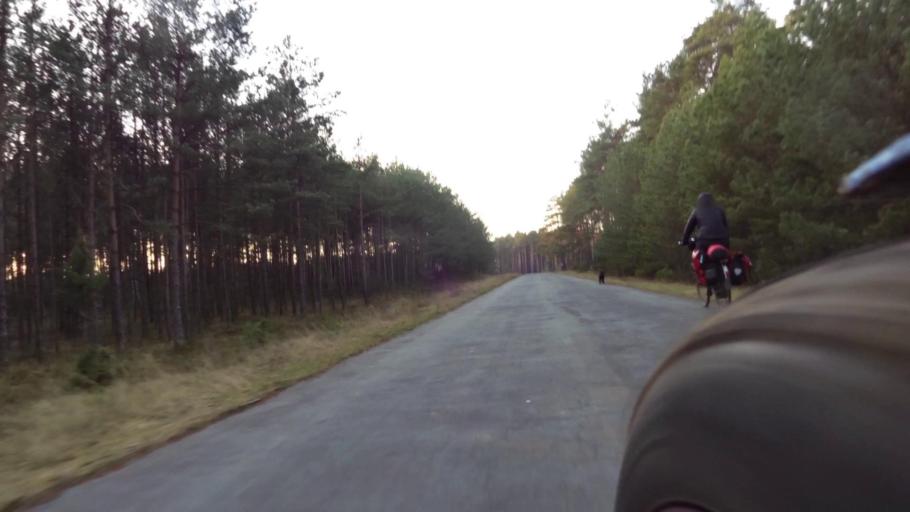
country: PL
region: West Pomeranian Voivodeship
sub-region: Powiat szczecinecki
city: Borne Sulinowo
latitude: 53.5693
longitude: 16.5870
